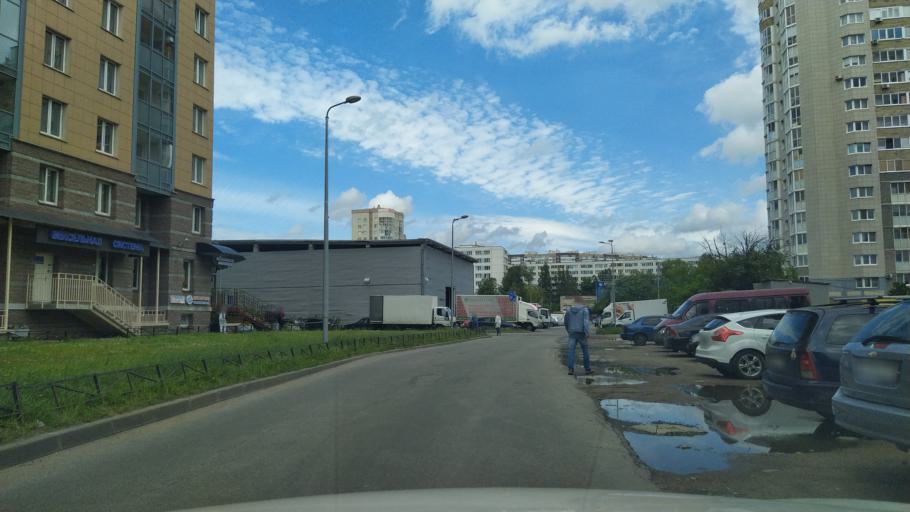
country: RU
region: Leningrad
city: Akademicheskoe
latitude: 60.0131
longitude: 30.3891
